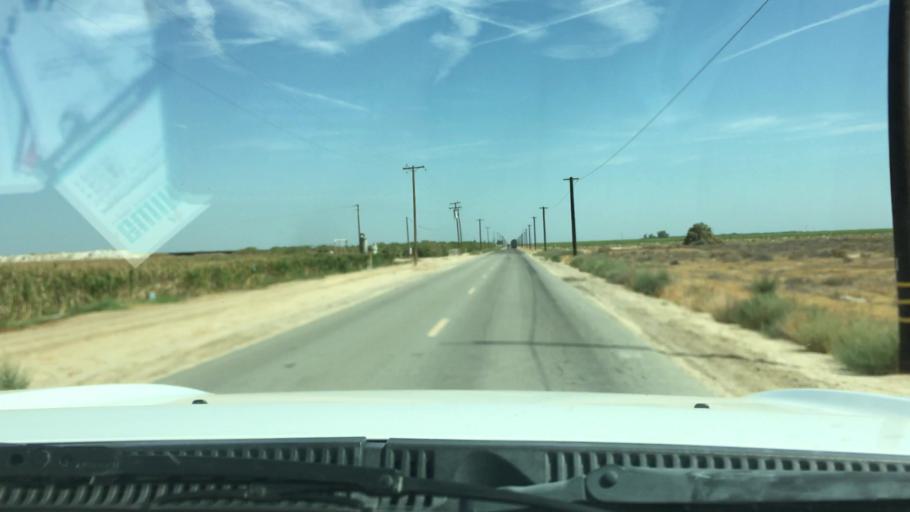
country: US
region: California
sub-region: Kern County
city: Shafter
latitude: 35.4477
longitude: -119.3681
